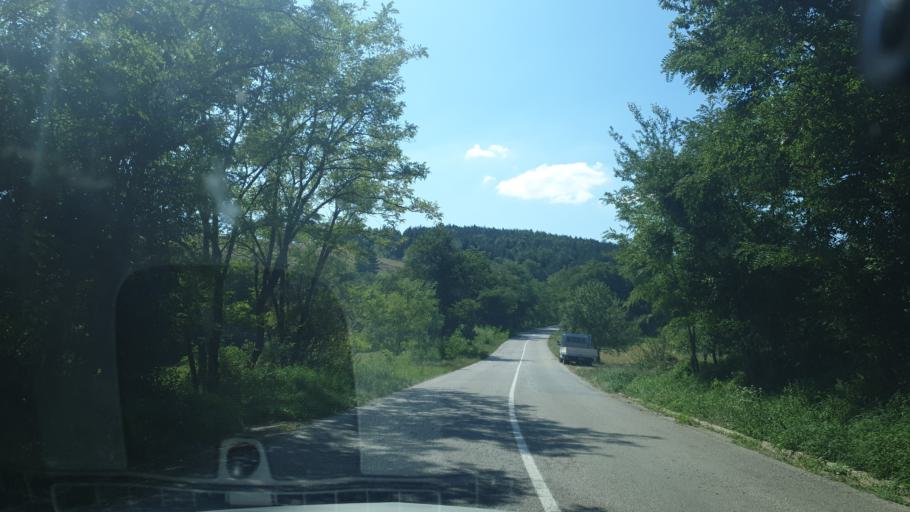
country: RS
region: Central Serbia
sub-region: Zlatiborski Okrug
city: Kosjeric
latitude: 44.0484
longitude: 20.0279
